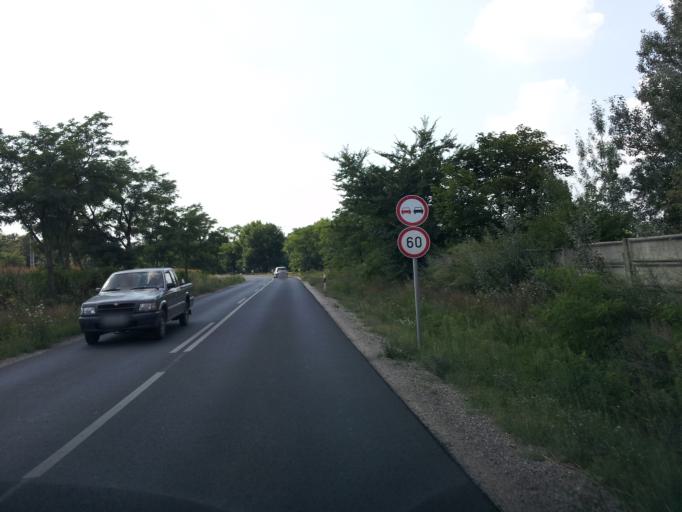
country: HU
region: Pest
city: Toekoel
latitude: 47.3398
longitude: 18.9734
